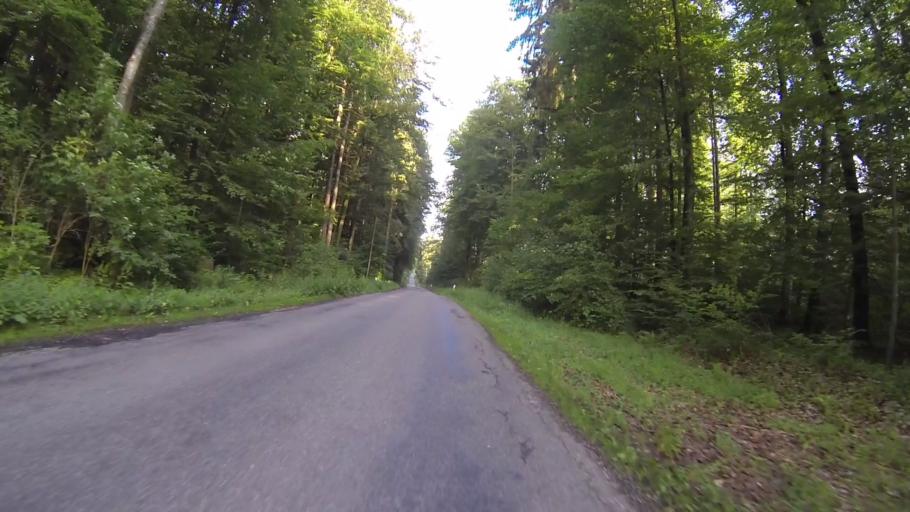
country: DE
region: Baden-Wuerttemberg
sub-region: Regierungsbezirk Stuttgart
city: Nattheim
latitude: 48.7241
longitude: 10.2466
